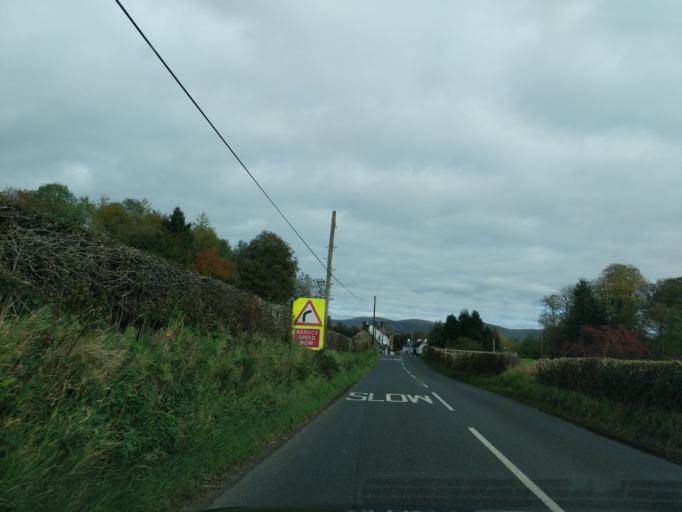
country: GB
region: Scotland
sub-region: Dumfries and Galloway
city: Thornhill
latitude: 55.2391
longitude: -3.7937
